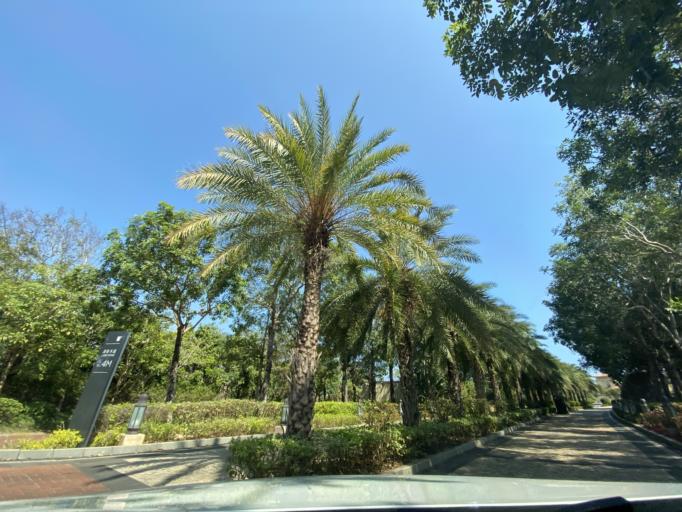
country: CN
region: Hainan
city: Haitangwan
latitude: 18.3508
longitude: 109.7362
